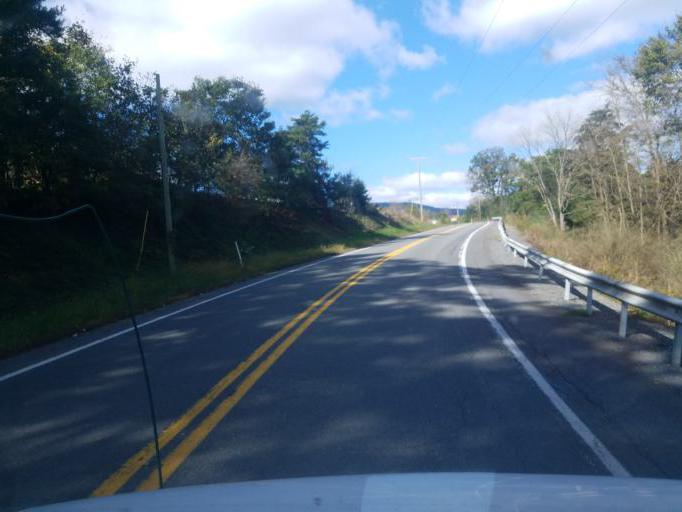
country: US
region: Pennsylvania
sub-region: Fulton County
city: McConnellsburg
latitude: 39.9917
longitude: -78.0821
